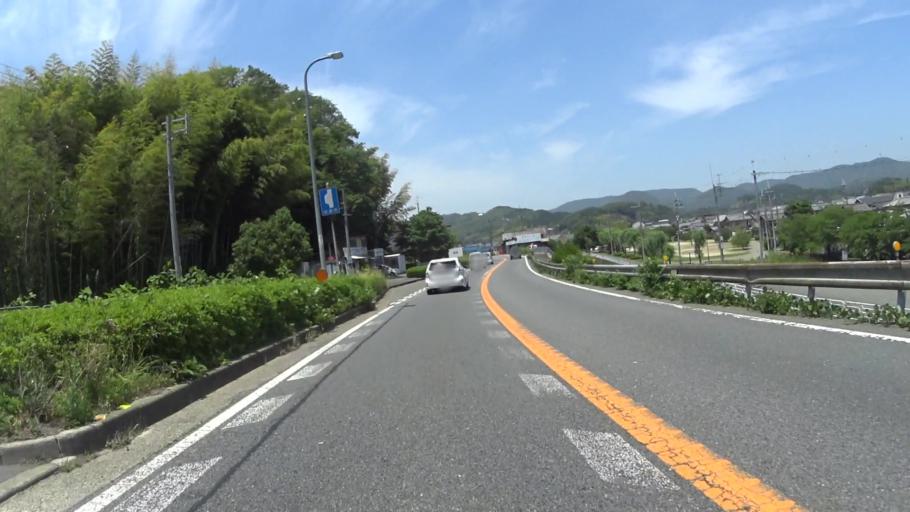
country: JP
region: Kyoto
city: Kameoka
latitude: 35.1075
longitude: 135.4780
